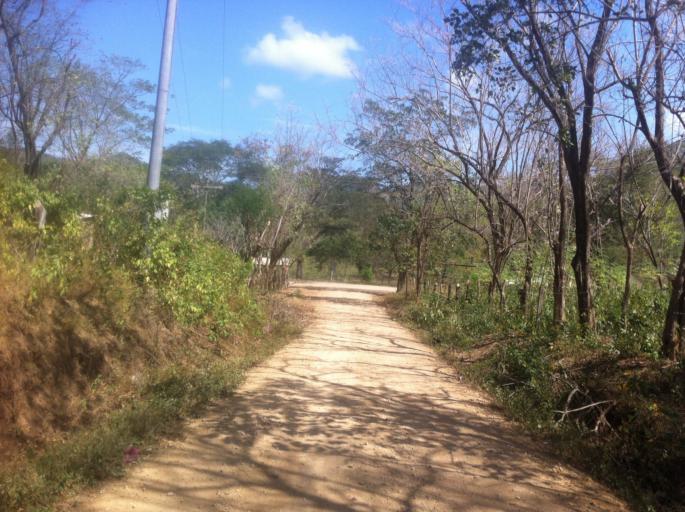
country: NI
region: Rivas
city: Tola
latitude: 11.4096
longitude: -86.0110
